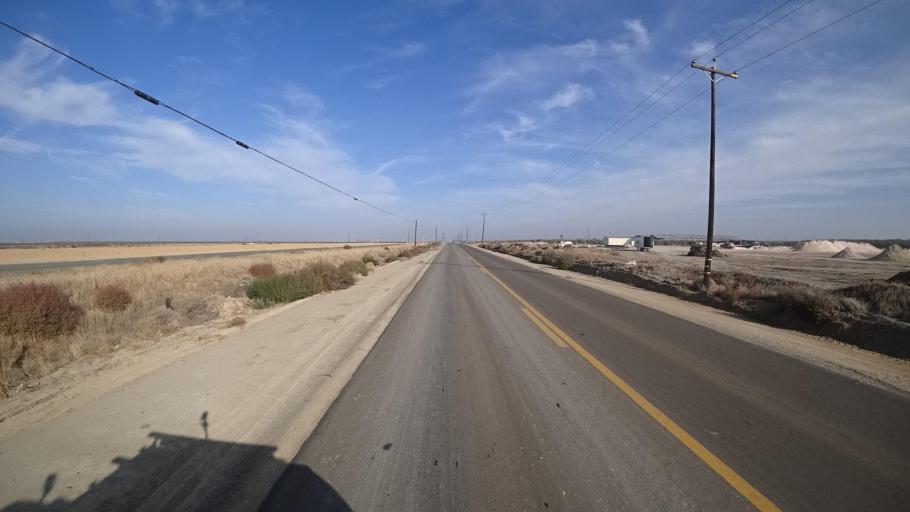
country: US
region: California
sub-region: Kern County
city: McFarland
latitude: 35.6427
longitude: -119.2045
